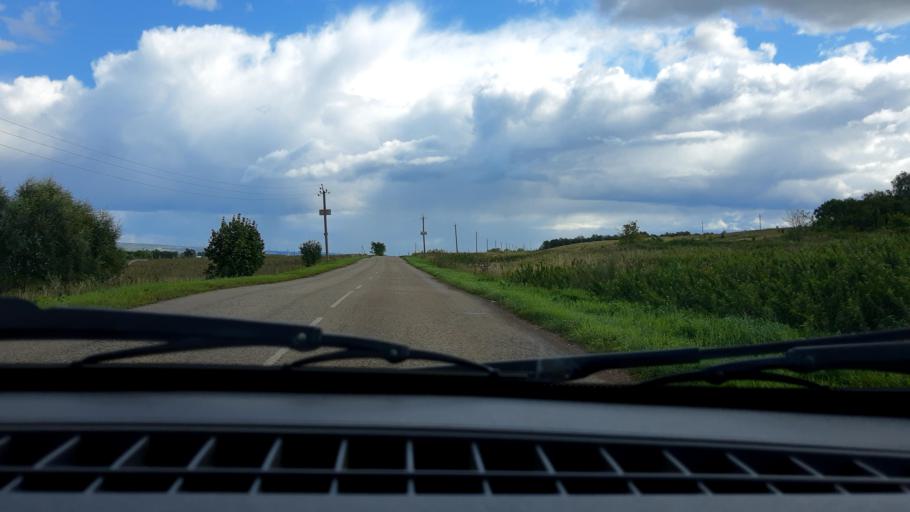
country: RU
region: Bashkortostan
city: Blagoveshchensk
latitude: 54.9396
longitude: 55.8883
